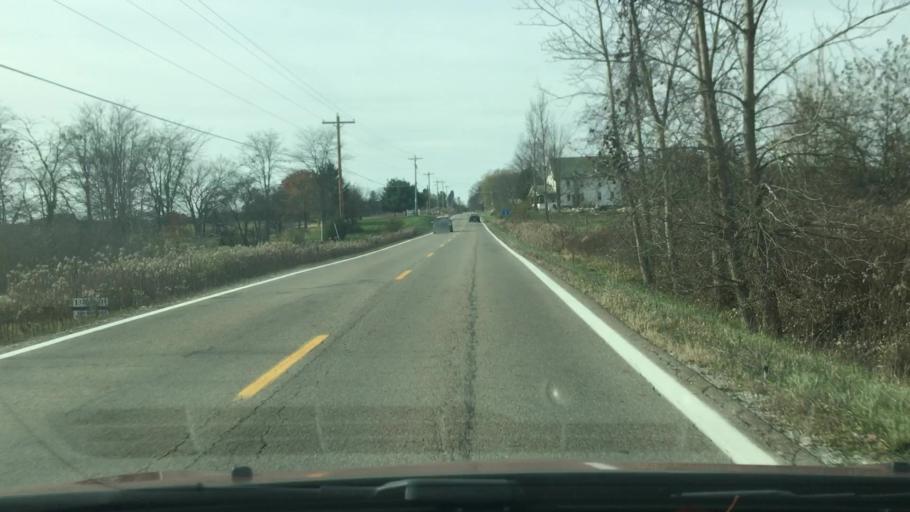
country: US
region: Ohio
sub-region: Delaware County
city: Sunbury
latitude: 40.3239
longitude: -82.8221
